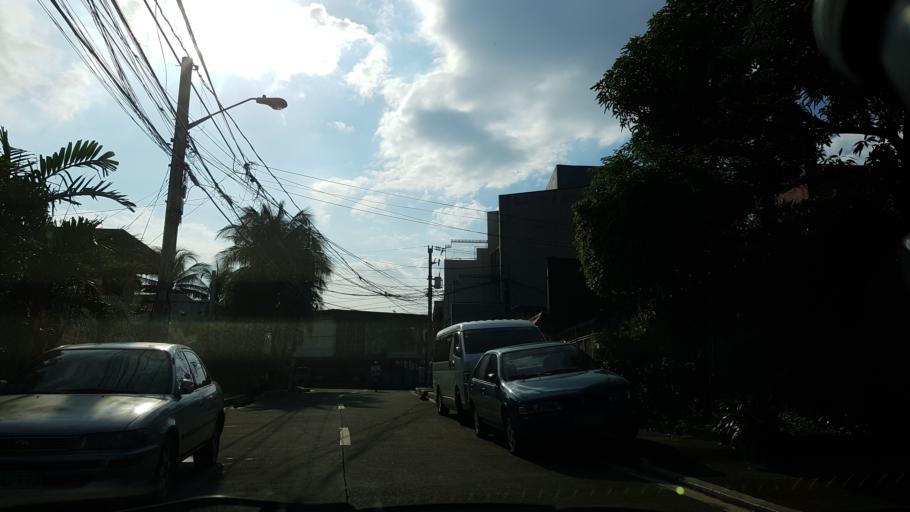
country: PH
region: Metro Manila
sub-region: Quezon City
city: Quezon City
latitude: 14.6416
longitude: 121.0502
